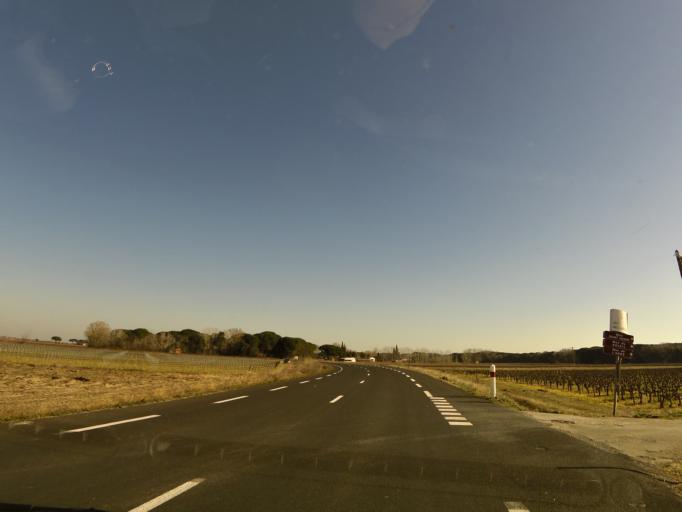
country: FR
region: Languedoc-Roussillon
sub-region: Departement du Gard
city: Aigues-Mortes
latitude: 43.5863
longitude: 4.2261
